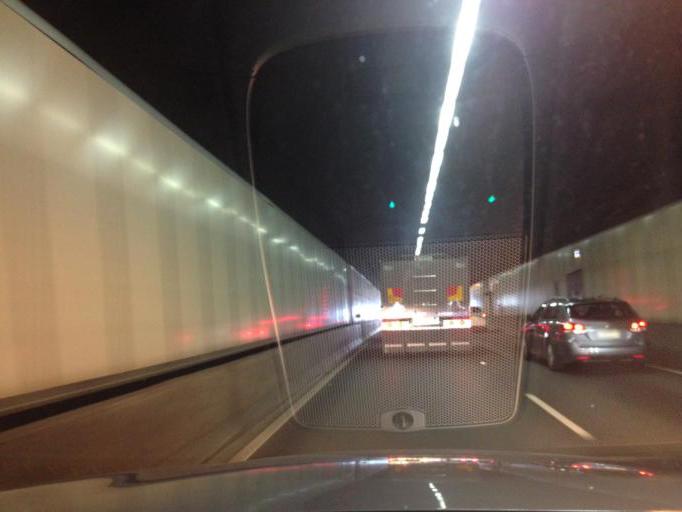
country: AU
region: New South Wales
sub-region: Rockdale
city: Arncliffe
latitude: -33.9427
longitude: 151.1596
